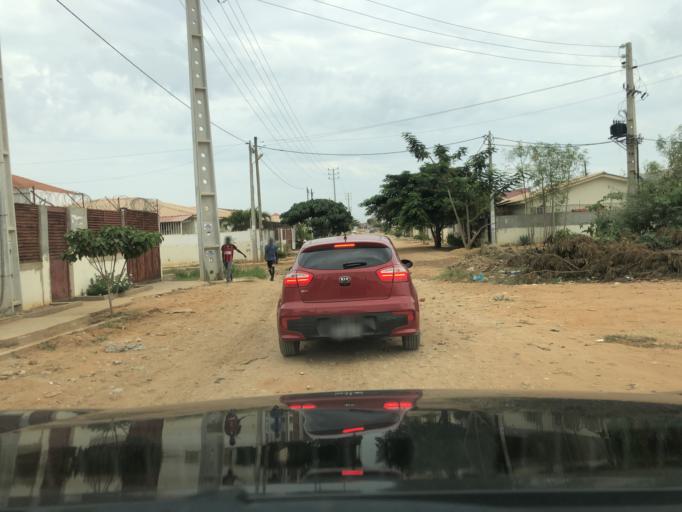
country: AO
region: Luanda
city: Luanda
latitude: -8.9370
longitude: 13.2432
